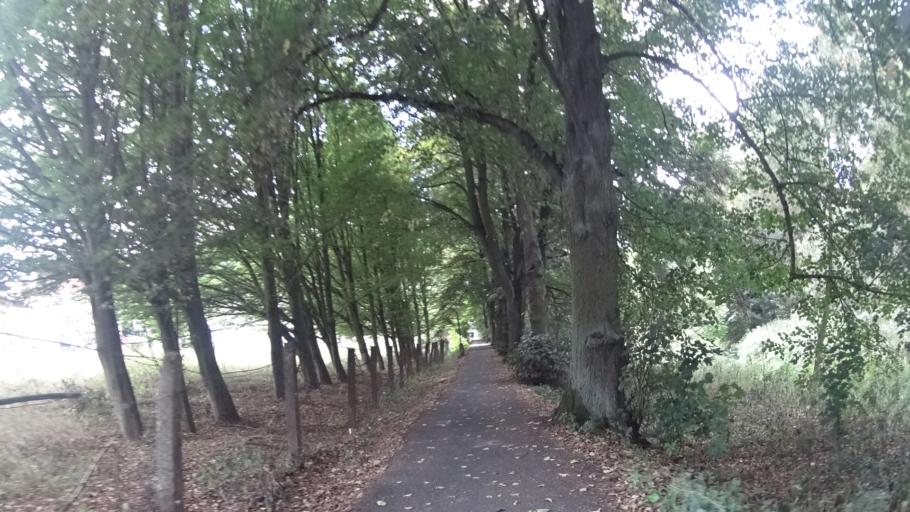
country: CZ
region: Pardubicky
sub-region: Okres Usti nad Orlici
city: Usti nad Orlici
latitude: 49.9729
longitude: 16.3859
